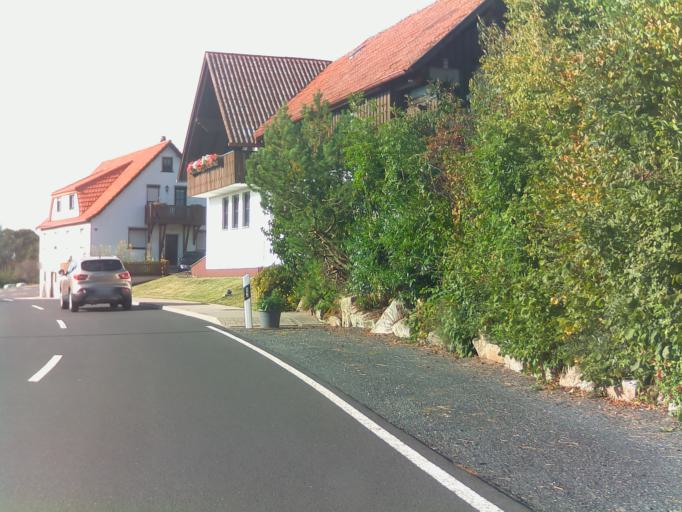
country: DE
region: Hesse
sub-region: Regierungsbezirk Kassel
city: Poppenhausen
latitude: 50.5375
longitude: 9.8651
